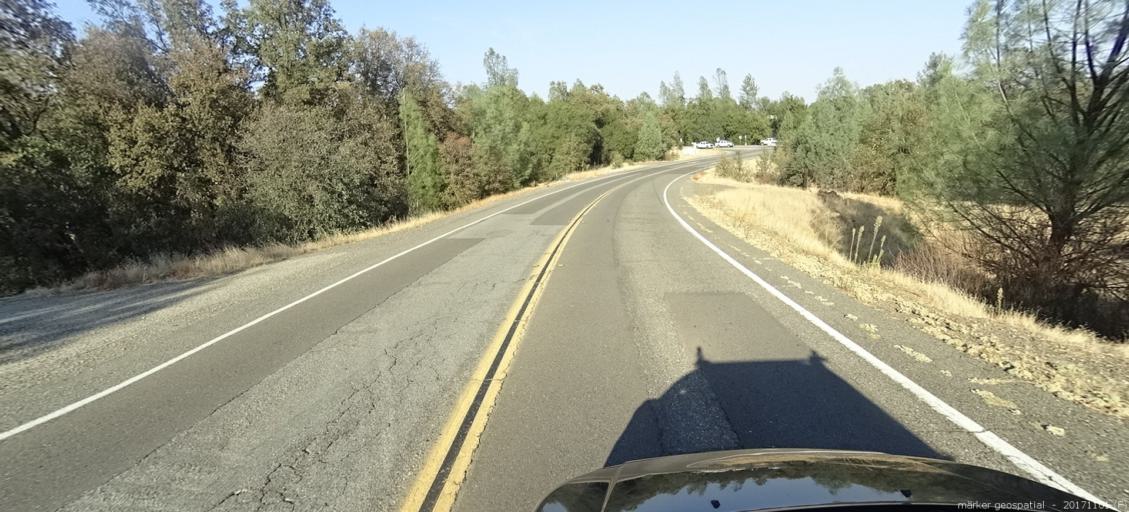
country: US
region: California
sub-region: Shasta County
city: Shasta Lake
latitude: 40.6221
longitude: -122.3211
